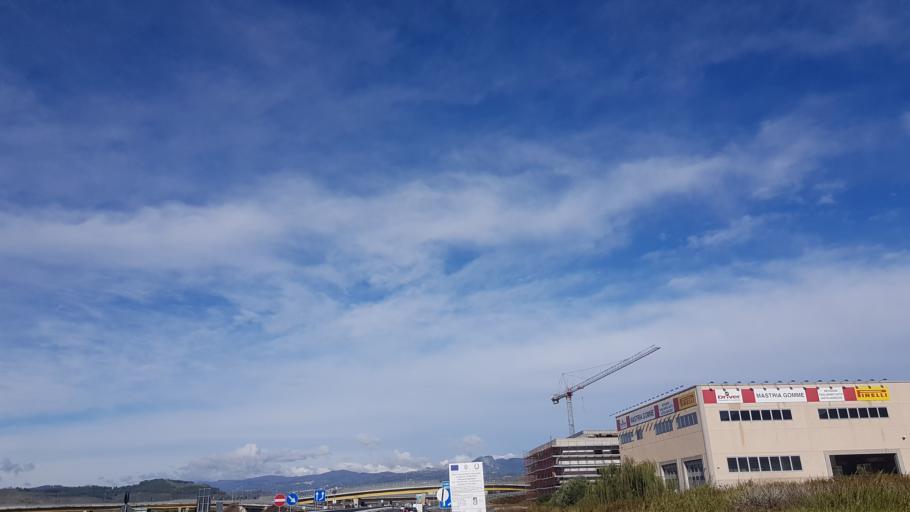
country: IT
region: Calabria
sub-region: Provincia di Catanzaro
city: Roccelletta
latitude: 38.8471
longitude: 16.5815
